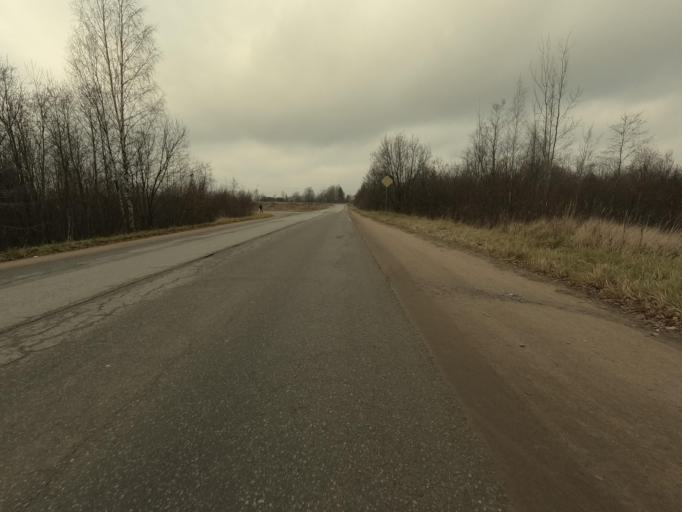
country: RU
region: Leningrad
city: Lyuban'
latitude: 59.4848
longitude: 31.2651
